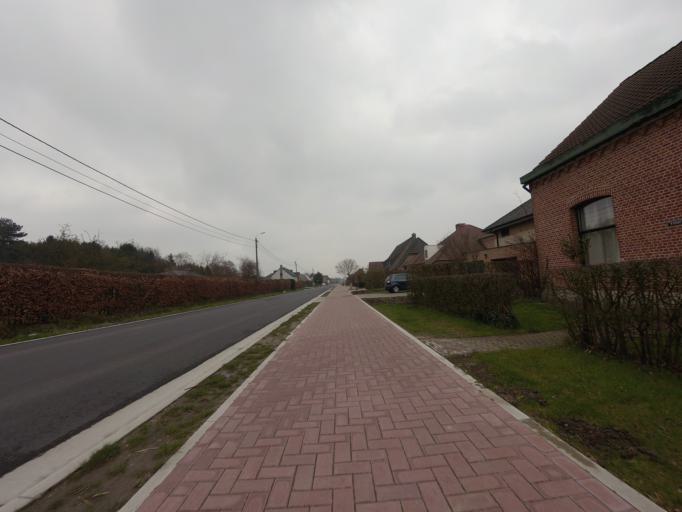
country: BE
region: Flanders
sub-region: Provincie Antwerpen
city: Putte
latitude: 51.0578
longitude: 4.5940
